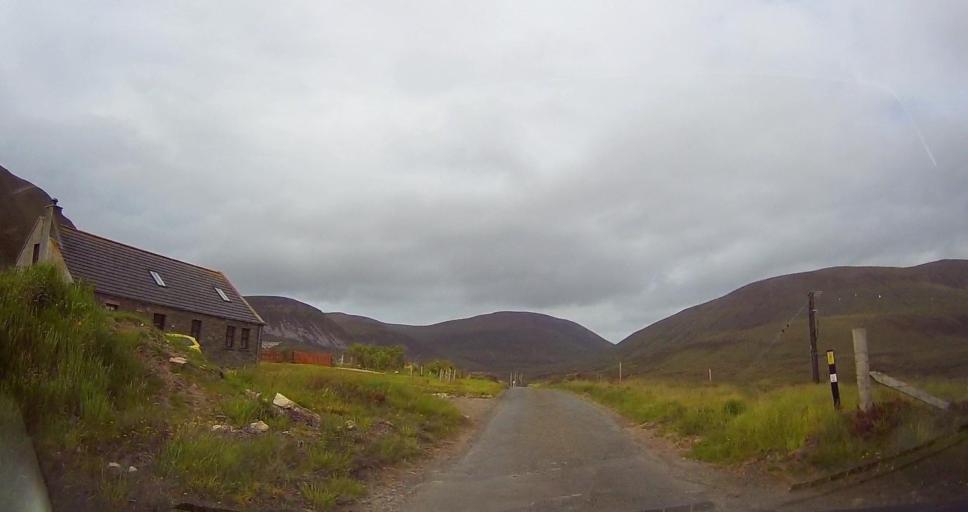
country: GB
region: Scotland
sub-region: Orkney Islands
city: Stromness
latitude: 58.8761
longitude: -3.3865
